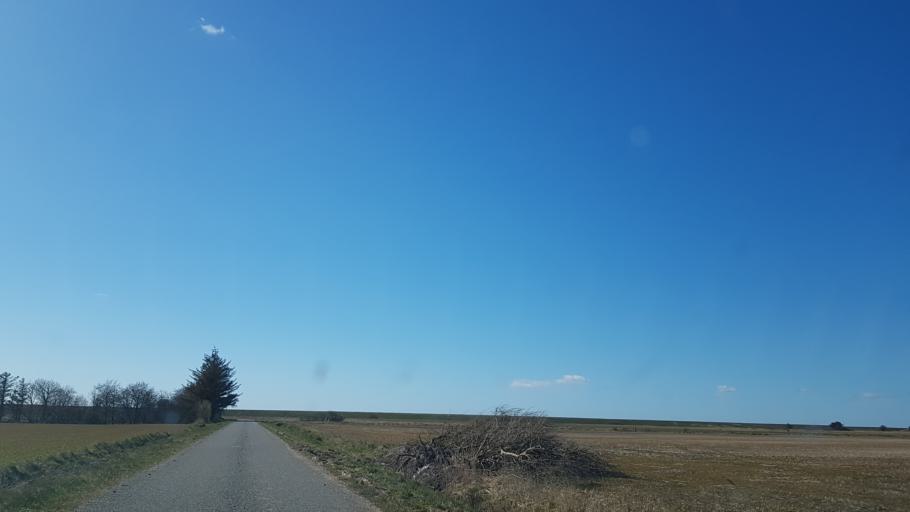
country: DK
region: South Denmark
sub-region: Esbjerg Kommune
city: Ribe
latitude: 55.2595
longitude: 8.6728
